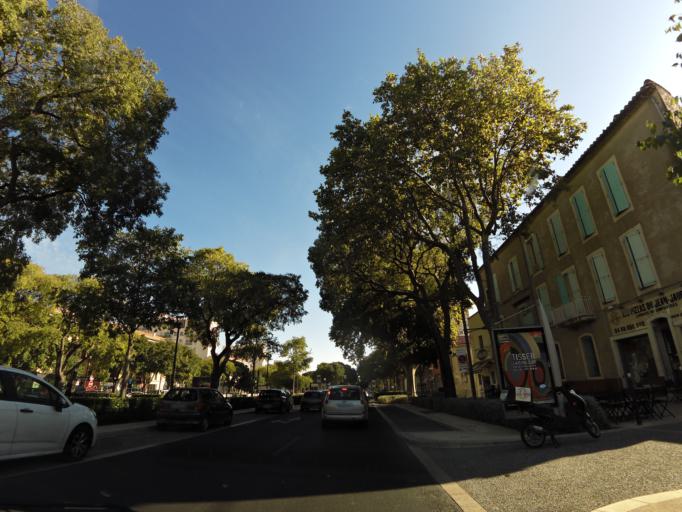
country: FR
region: Languedoc-Roussillon
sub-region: Departement du Gard
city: Nimes
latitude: 43.8338
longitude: 4.3512
